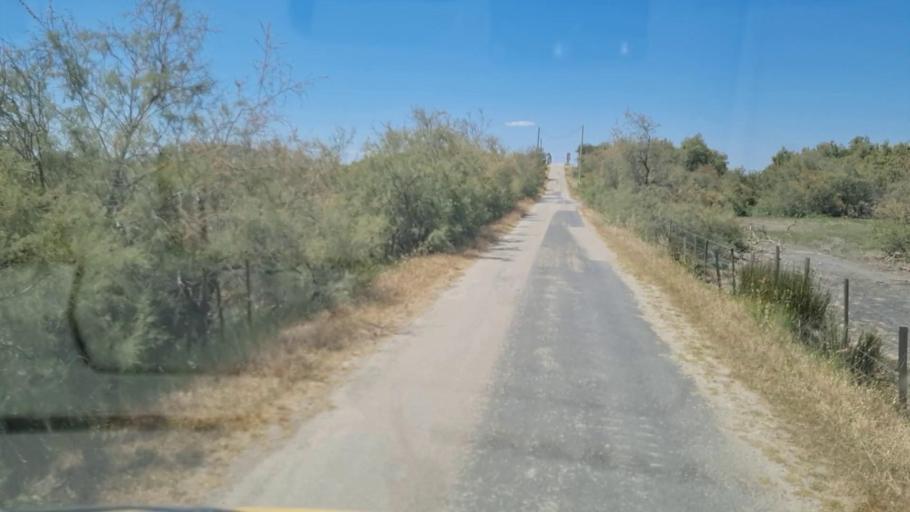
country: FR
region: Languedoc-Roussillon
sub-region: Departement du Gard
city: Le Cailar
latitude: 43.6181
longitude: 4.2612
